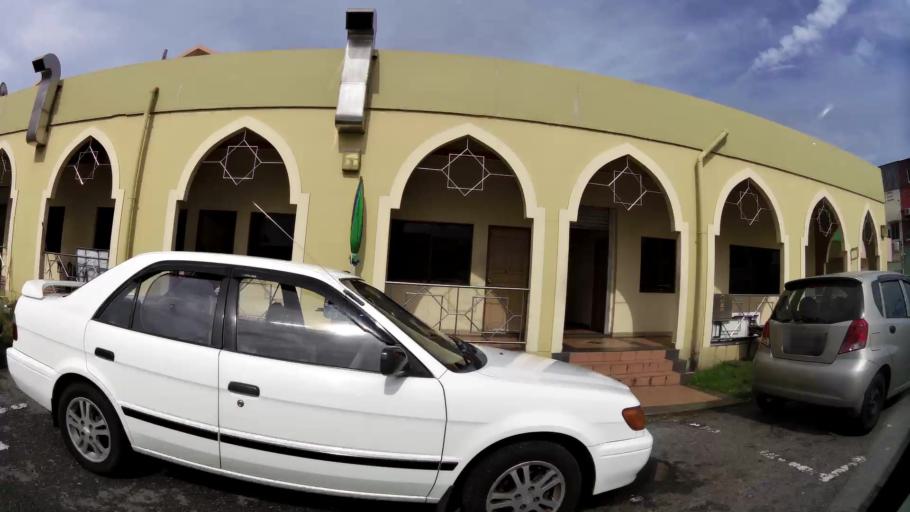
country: BN
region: Belait
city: Seria
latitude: 4.6145
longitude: 114.3312
